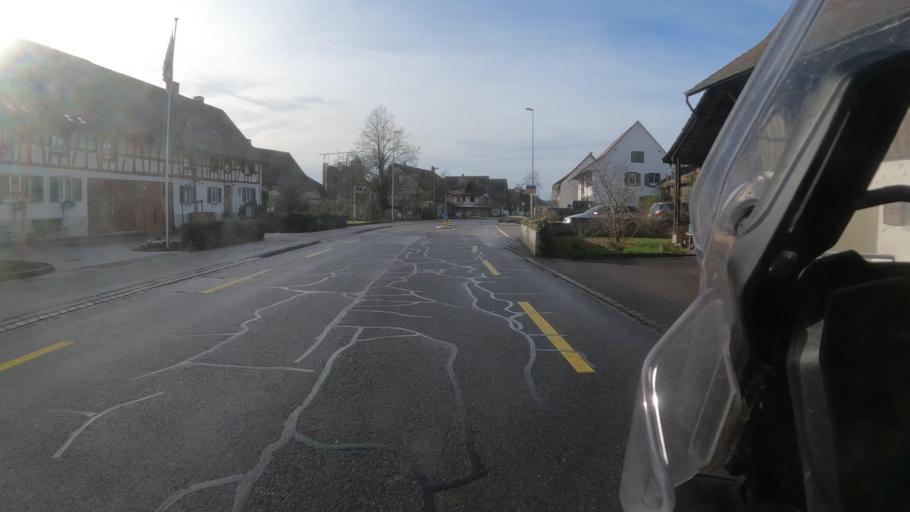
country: CH
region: Zurich
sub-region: Bezirk Buelach
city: Rafz
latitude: 47.6128
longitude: 8.5456
